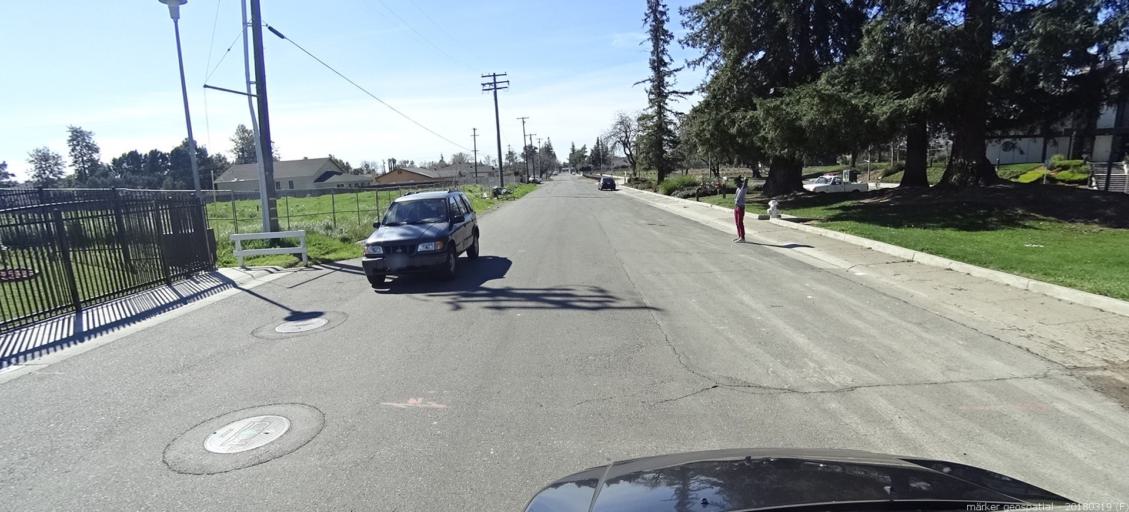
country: US
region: California
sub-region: Sacramento County
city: Parkway
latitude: 38.4874
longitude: -121.4388
